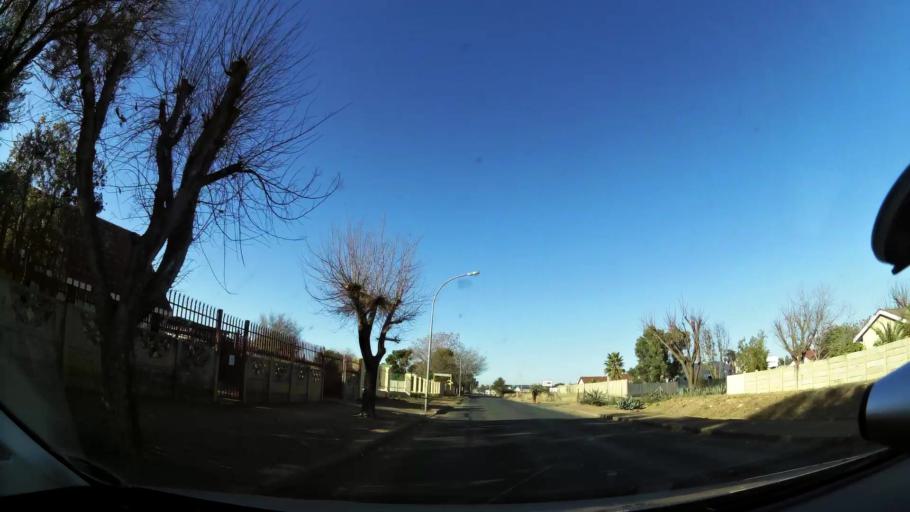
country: ZA
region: Northern Cape
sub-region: Frances Baard District Municipality
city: Kimberley
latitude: -28.7408
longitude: 24.7309
